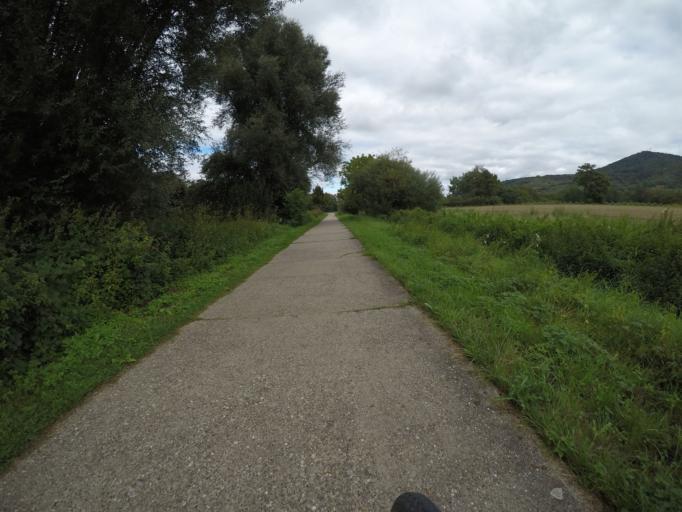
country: DE
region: Hesse
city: Zwingenberg
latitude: 49.7088
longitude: 8.6090
